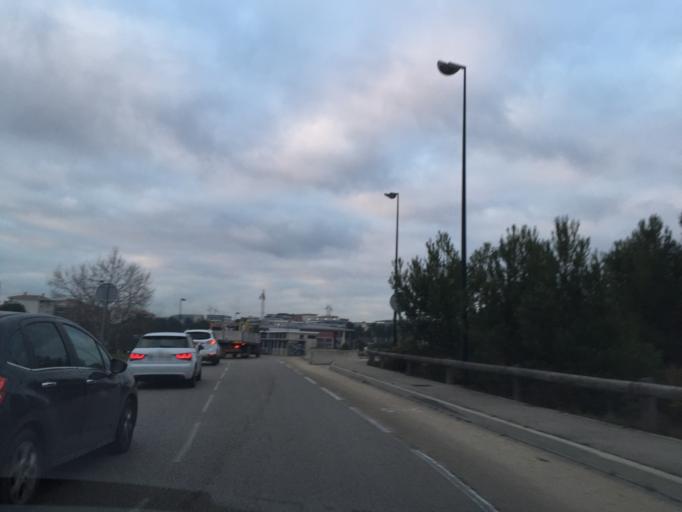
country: FR
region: Provence-Alpes-Cote d'Azur
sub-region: Departement des Bouches-du-Rhone
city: Ventabren
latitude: 43.4943
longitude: 5.3421
